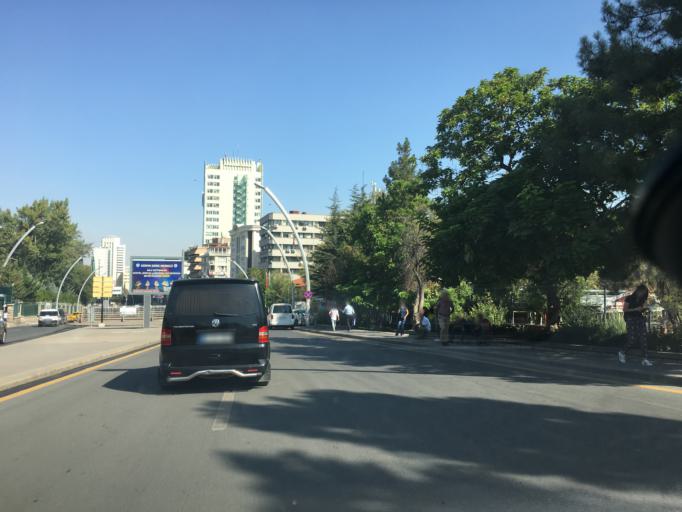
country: TR
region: Ankara
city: Cankaya
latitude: 39.9015
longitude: 32.8594
